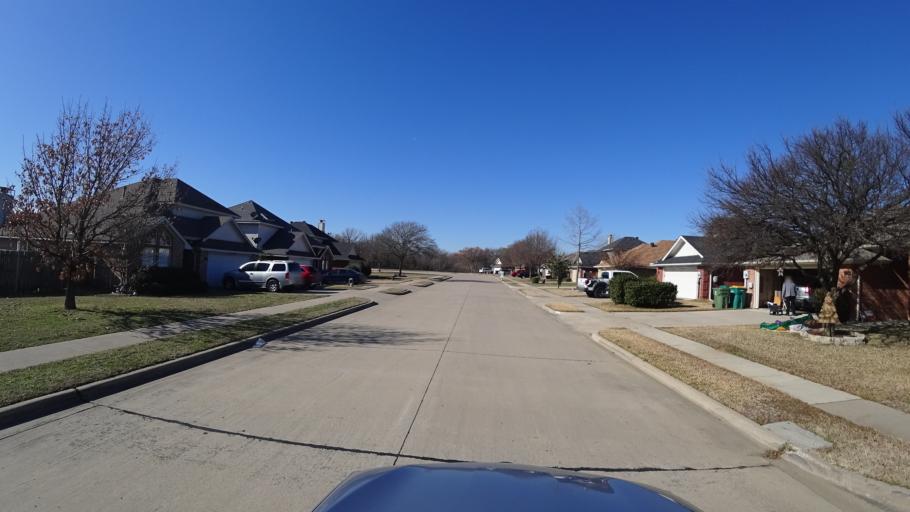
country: US
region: Texas
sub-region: Denton County
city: Lewisville
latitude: 33.0229
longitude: -97.0241
